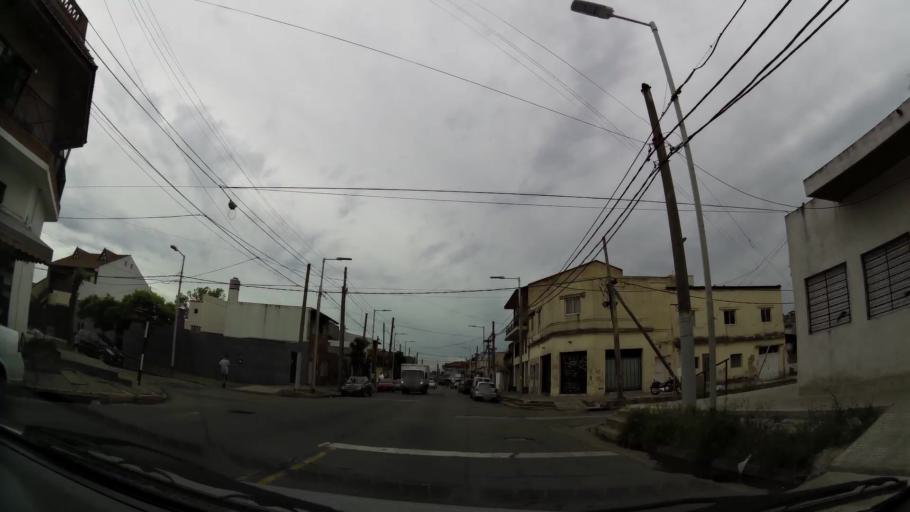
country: AR
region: Buenos Aires
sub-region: Partido de Avellaneda
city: Avellaneda
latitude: -34.6809
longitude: -58.3694
